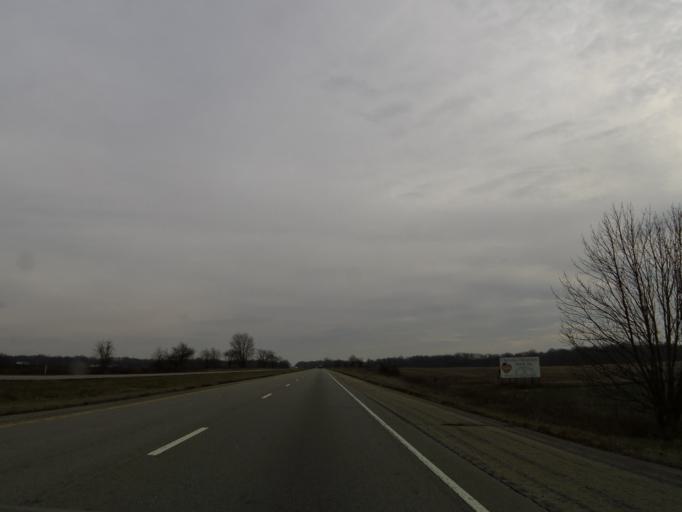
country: US
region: Indiana
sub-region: Fountain County
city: Covington
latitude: 40.1182
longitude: -87.4819
